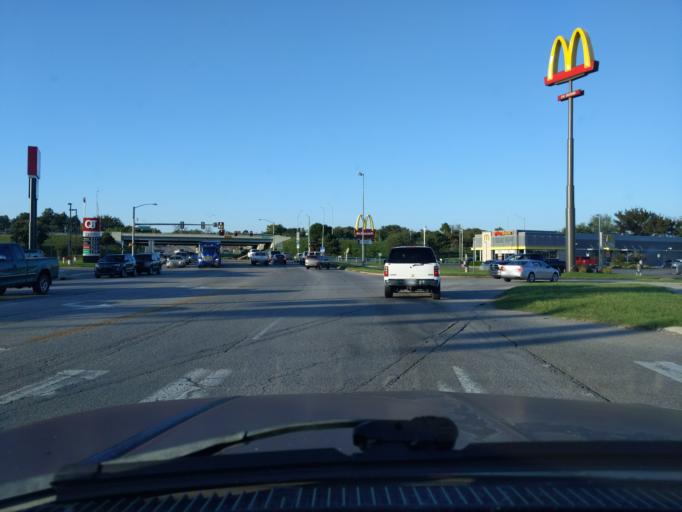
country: US
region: Oklahoma
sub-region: Tulsa County
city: Sand Springs
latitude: 36.1352
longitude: -96.1155
